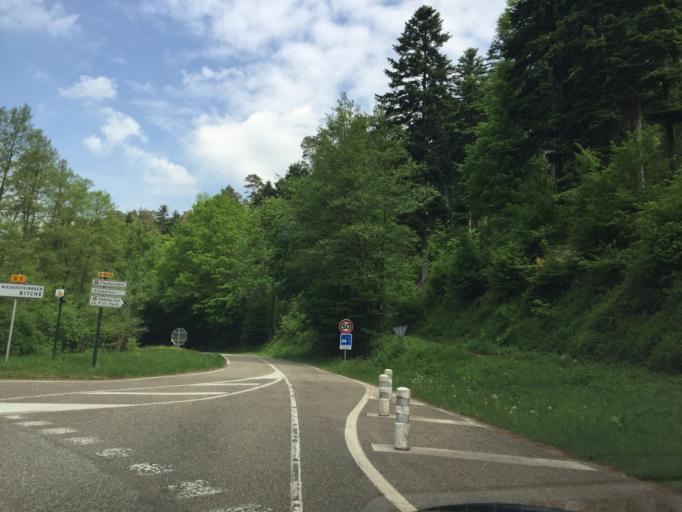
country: DE
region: Rheinland-Pfalz
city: Hirschthal
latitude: 49.0258
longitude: 7.7708
